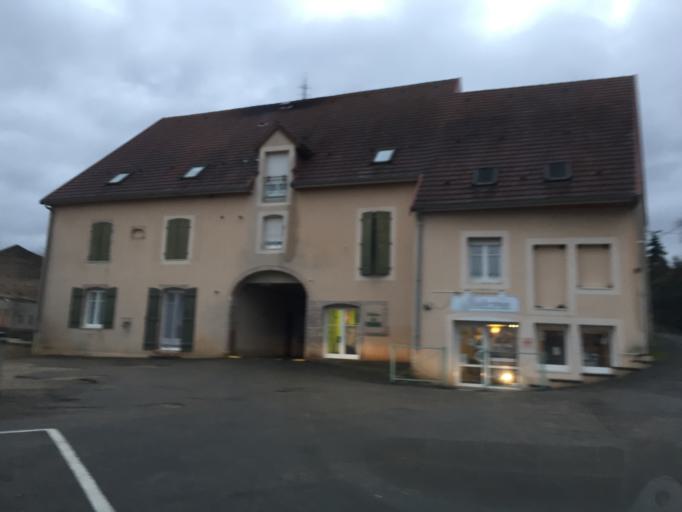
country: FR
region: Franche-Comte
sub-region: Departement du Jura
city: Champvans
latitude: 47.1265
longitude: 5.4536
